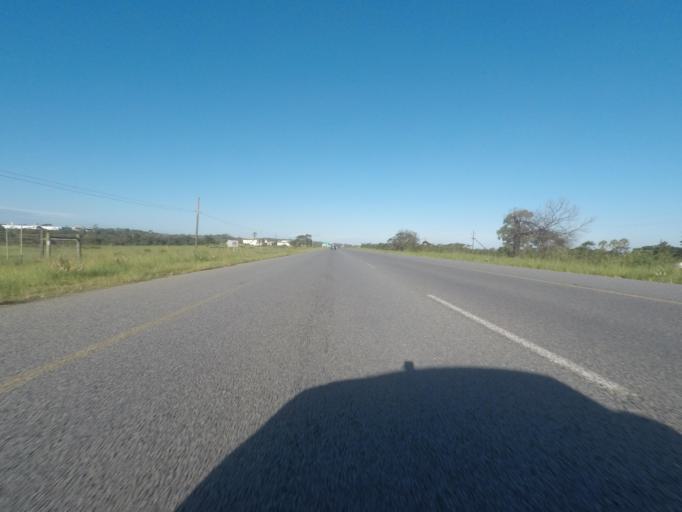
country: ZA
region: Eastern Cape
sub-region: Buffalo City Metropolitan Municipality
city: East London
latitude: -33.0551
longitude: 27.8025
